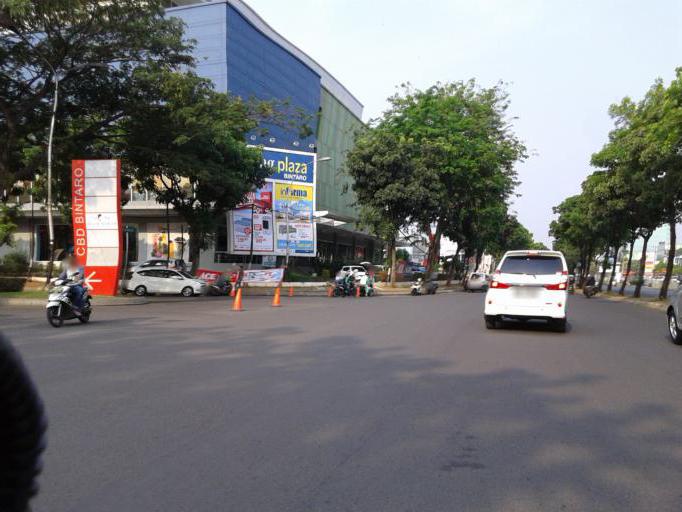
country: ID
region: Banten
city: South Tangerang
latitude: -6.2790
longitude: 106.7192
